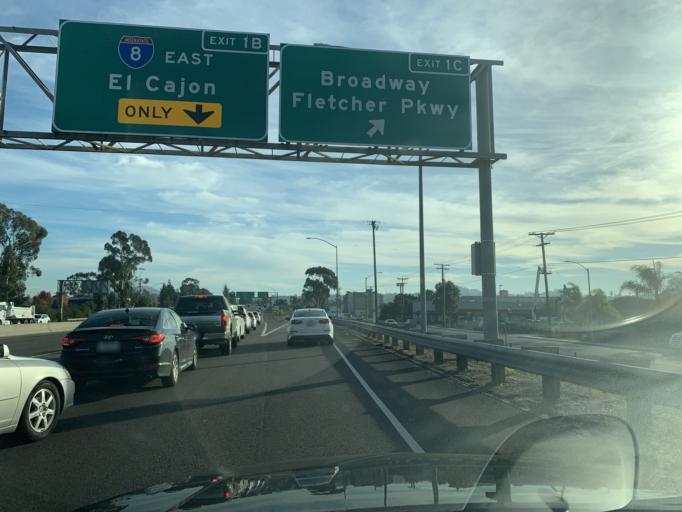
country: US
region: California
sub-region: San Diego County
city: El Cajon
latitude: 32.8122
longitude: -116.9621
